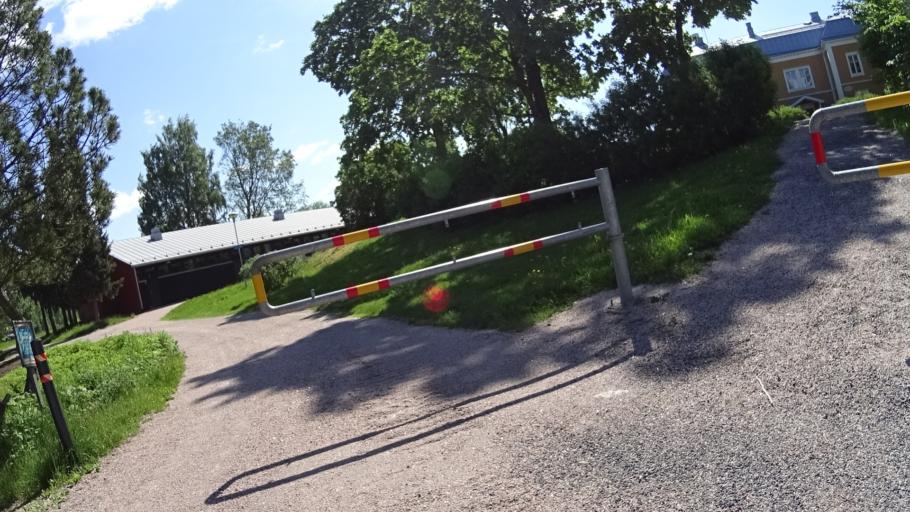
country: FI
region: Uusimaa
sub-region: Helsinki
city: Kauniainen
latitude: 60.3168
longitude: 24.6919
